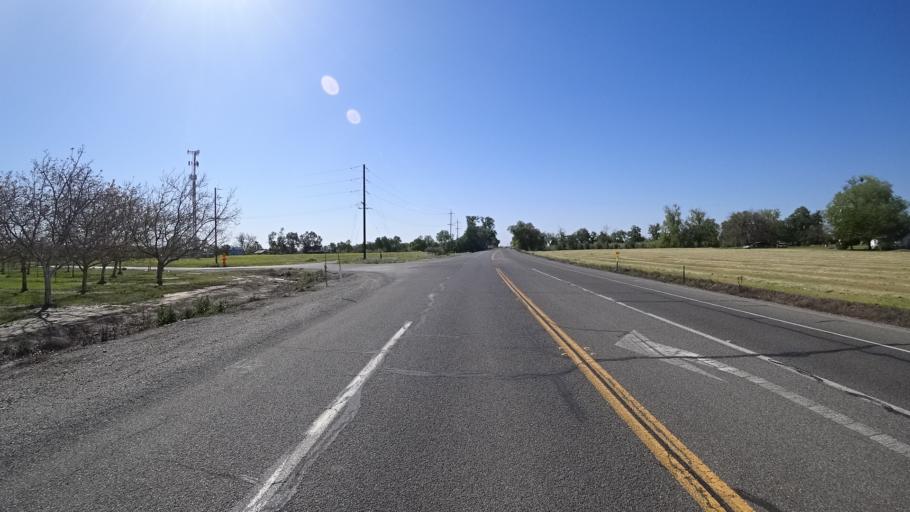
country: US
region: California
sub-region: Glenn County
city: Hamilton City
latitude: 39.7132
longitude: -122.0050
